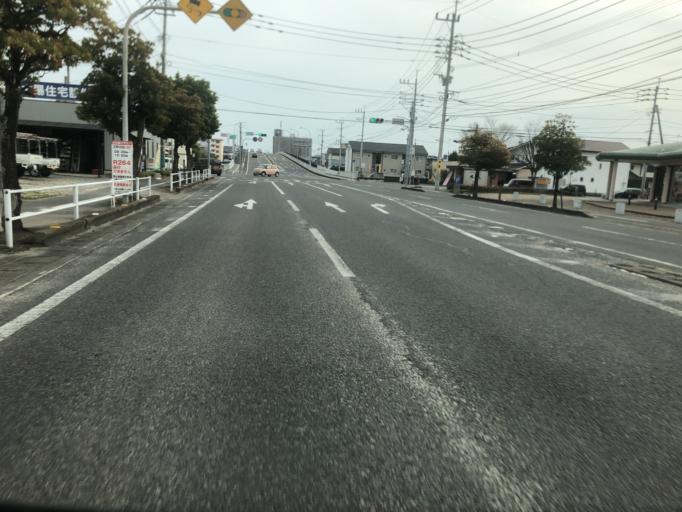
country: JP
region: Saga Prefecture
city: Saga-shi
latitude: 33.2623
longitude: 130.2725
